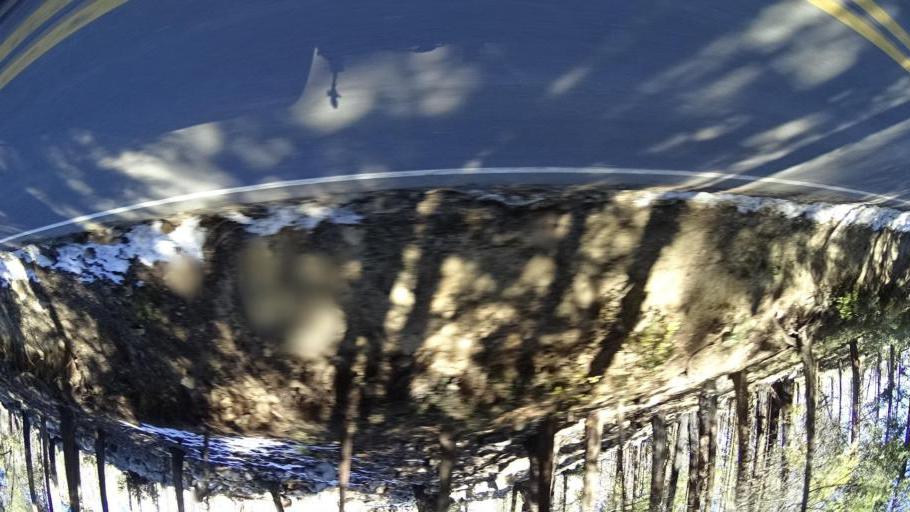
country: US
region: California
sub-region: Kern County
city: Alta Sierra
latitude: 35.7435
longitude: -118.5649
